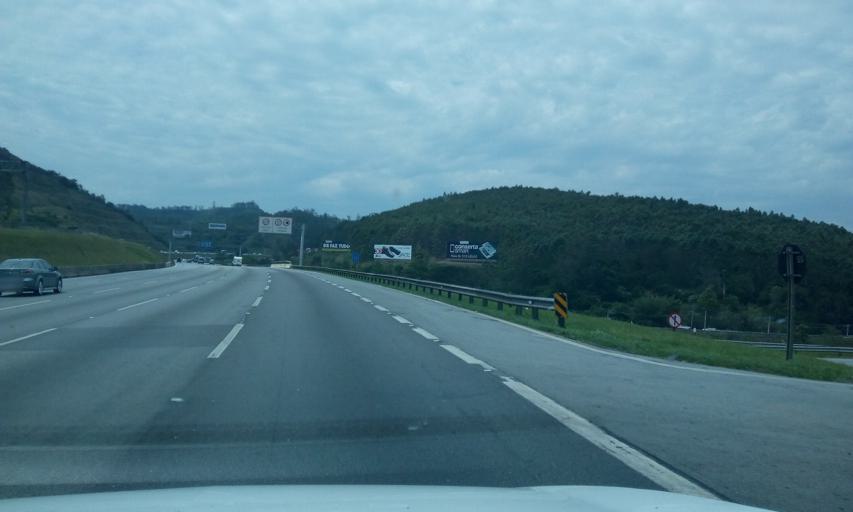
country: BR
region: Sao Paulo
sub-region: Varzea Paulista
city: Varzea Paulista
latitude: -23.2721
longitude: -46.8554
